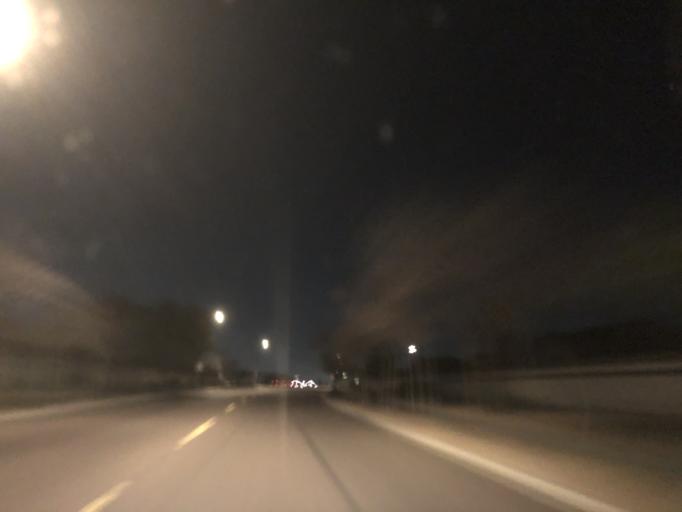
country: US
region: Arizona
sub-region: Maricopa County
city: Tolleson
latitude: 33.4100
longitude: -112.2742
